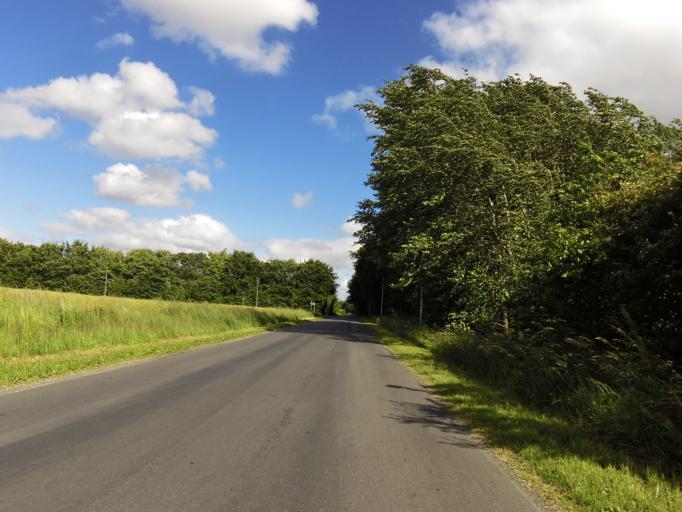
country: DK
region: South Denmark
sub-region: Kolding Kommune
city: Vamdrup
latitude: 55.3529
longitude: 9.2205
